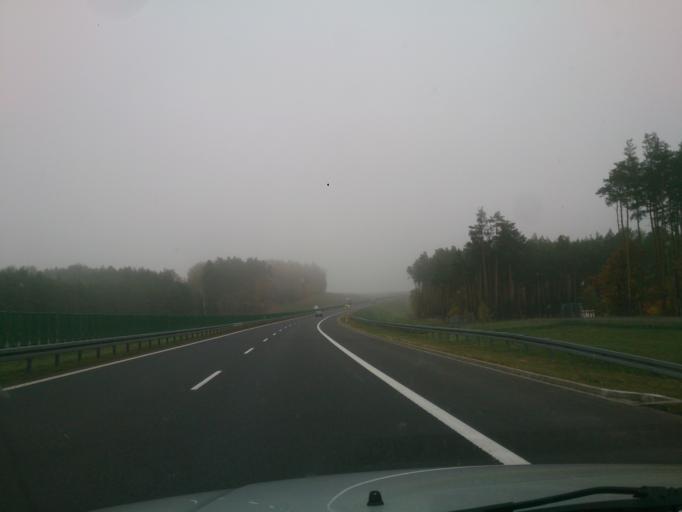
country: PL
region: Kujawsko-Pomorskie
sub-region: Powiat swiecki
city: Warlubie
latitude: 53.5267
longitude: 18.5997
